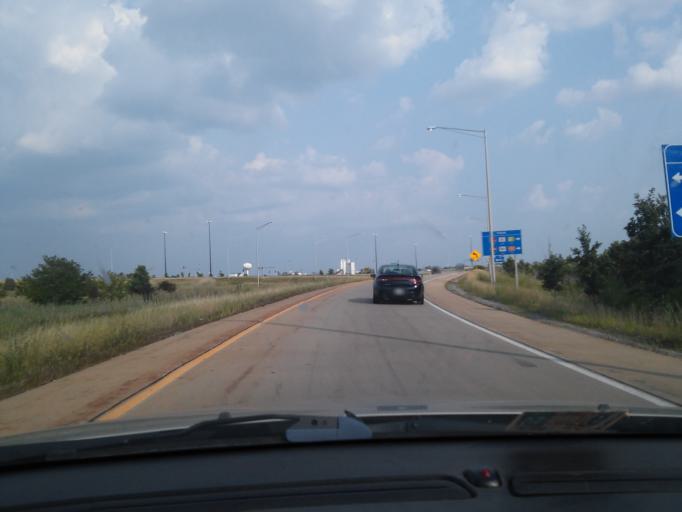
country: US
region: Illinois
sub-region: Cook County
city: Orland Hills
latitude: 41.5523
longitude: -87.8570
